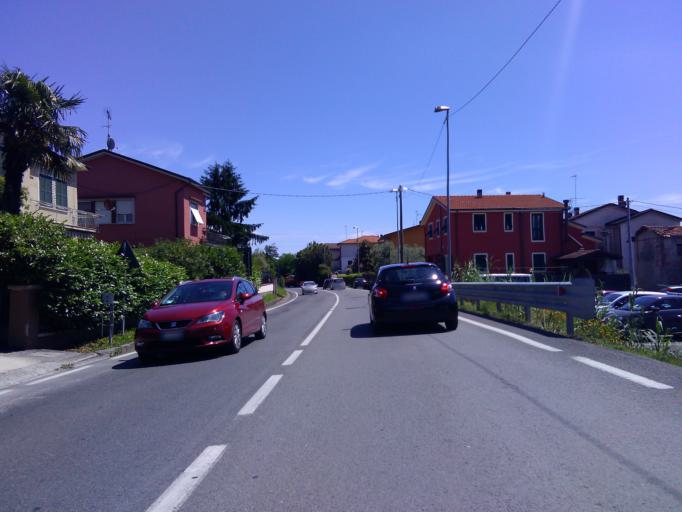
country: IT
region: Liguria
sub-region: Provincia di La Spezia
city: Santo Stefano di Magra
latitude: 44.1432
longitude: 9.9250
